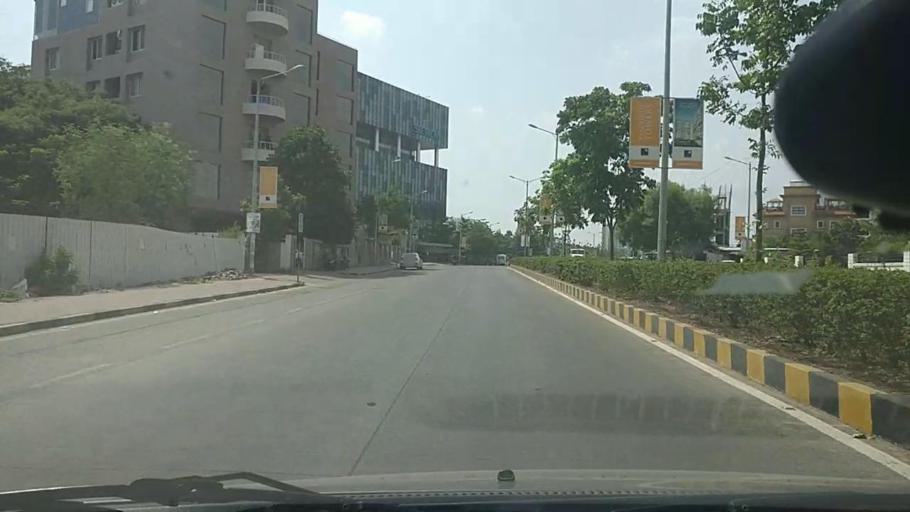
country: IN
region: Maharashtra
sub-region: Pune Division
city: Pimpri
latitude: 18.5676
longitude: 73.7757
